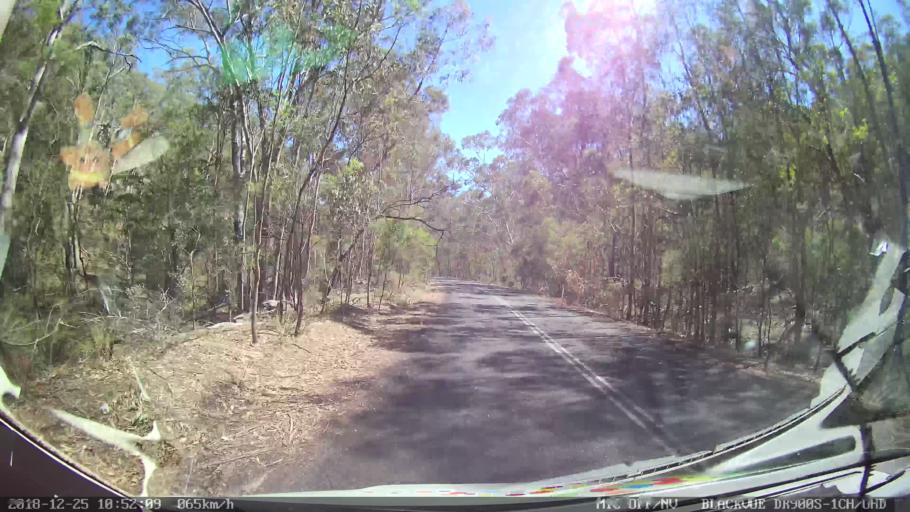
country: AU
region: New South Wales
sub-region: Upper Hunter Shire
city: Merriwa
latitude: -32.4314
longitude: 150.2733
